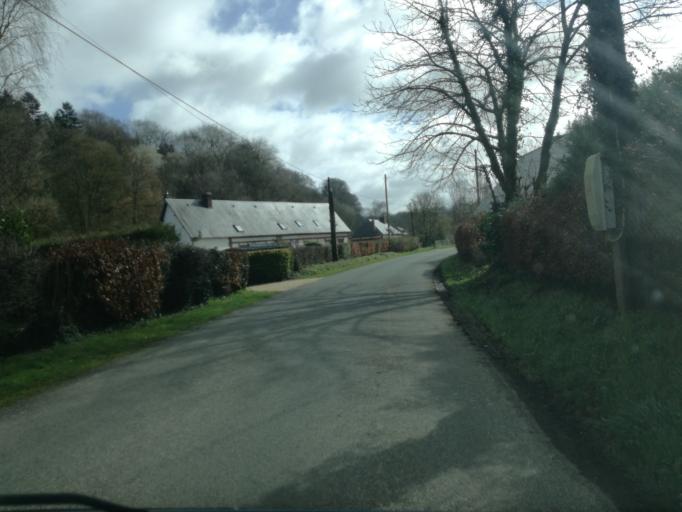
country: FR
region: Haute-Normandie
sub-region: Departement de la Seine-Maritime
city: Bretteville-du-Grand-Caux
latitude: 49.7000
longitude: 0.4588
